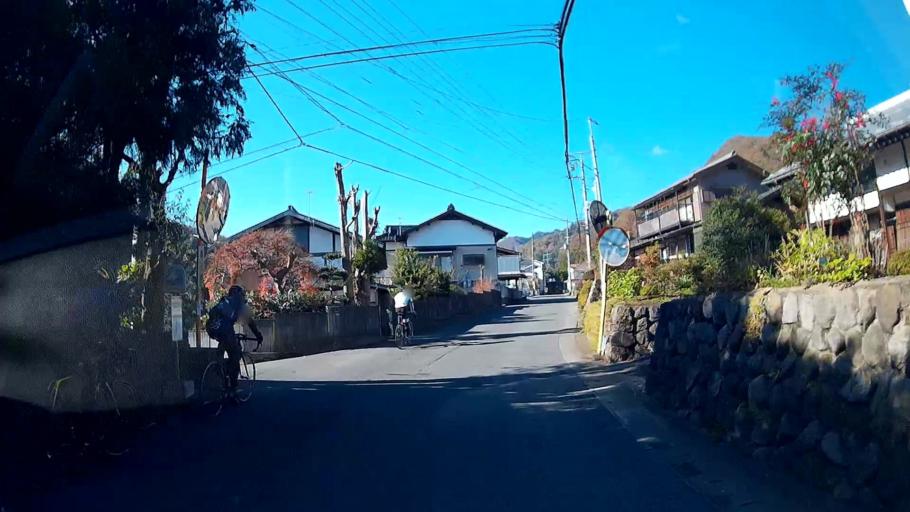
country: JP
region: Yamanashi
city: Uenohara
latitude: 35.5814
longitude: 139.1120
